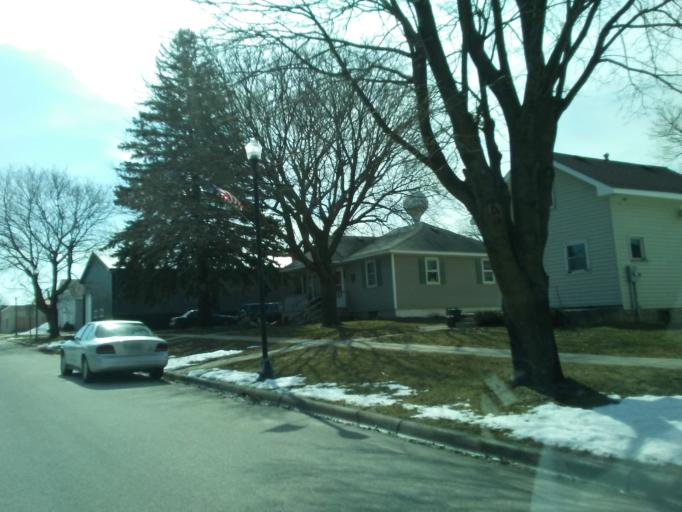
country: US
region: Minnesota
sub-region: Fillmore County
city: Preston
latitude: 43.7417
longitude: -92.1363
